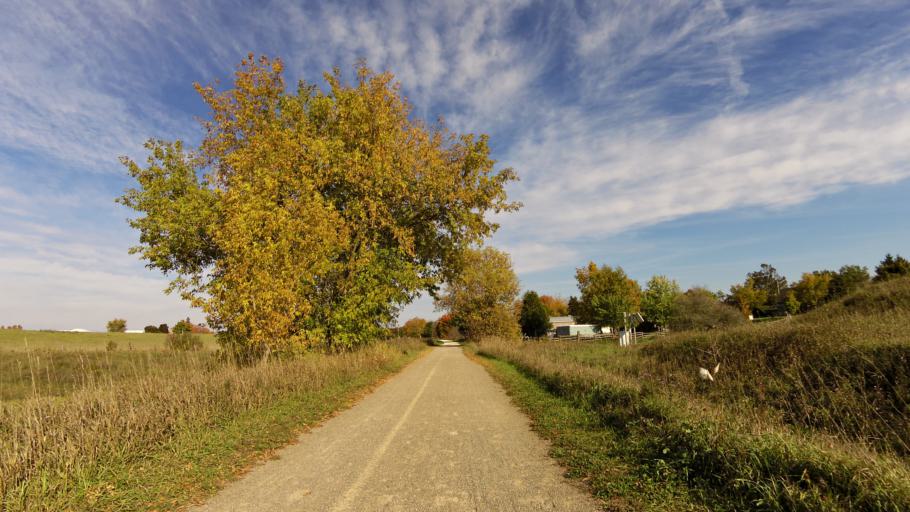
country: CA
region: Ontario
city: Orangeville
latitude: 43.7803
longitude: -80.0668
